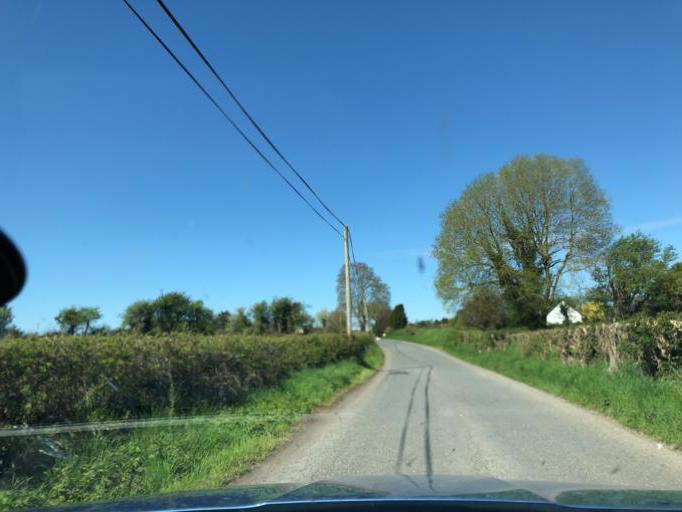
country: IE
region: Connaught
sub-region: County Galway
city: Portumna
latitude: 53.1789
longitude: -8.1802
